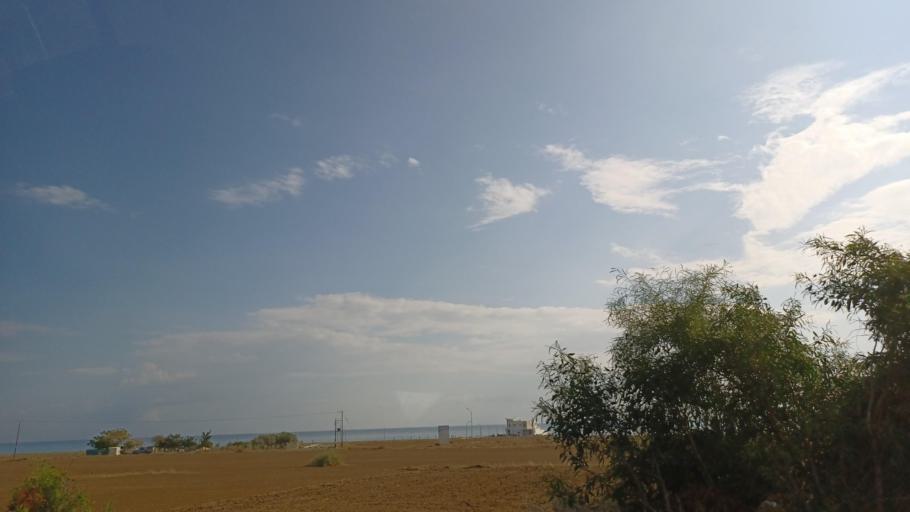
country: CY
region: Larnaka
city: Tersefanou
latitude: 34.8054
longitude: 33.5262
